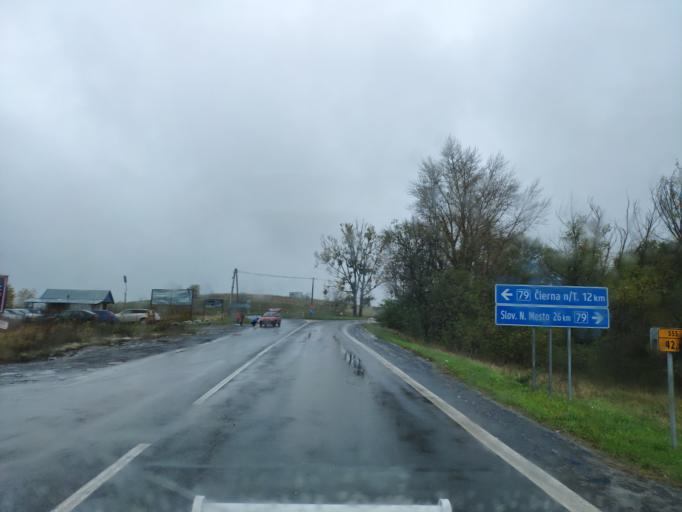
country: SK
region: Kosicky
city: Cierna nad Tisou
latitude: 48.4313
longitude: 21.9833
